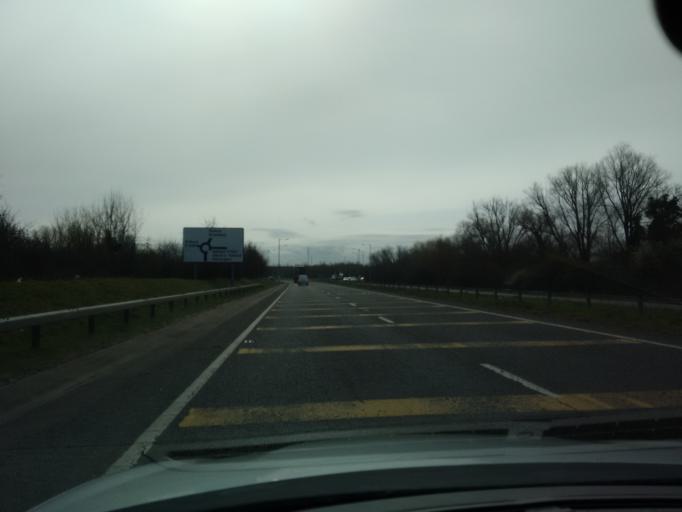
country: GB
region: England
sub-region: Warwickshire
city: Bidford-on-avon
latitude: 52.1624
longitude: -1.8826
